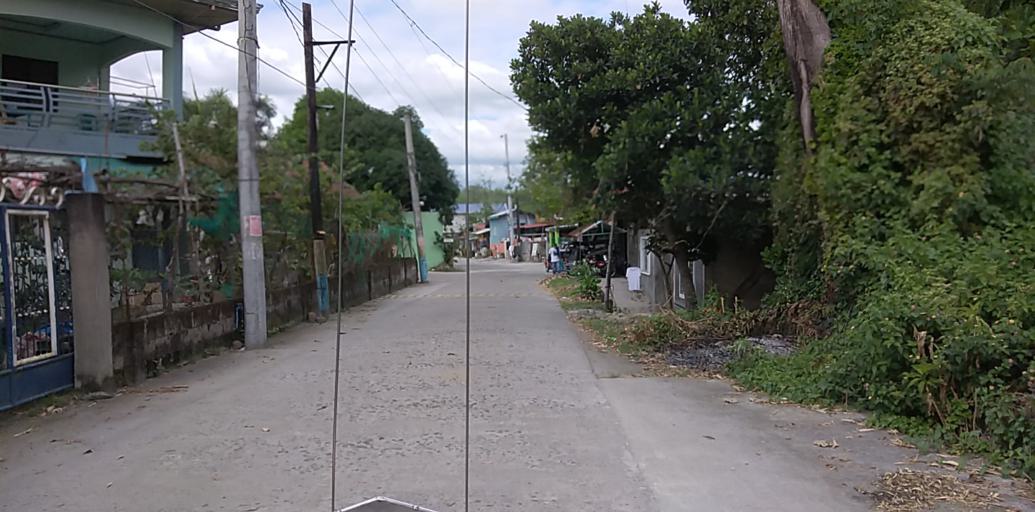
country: PH
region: Central Luzon
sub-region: Province of Pampanga
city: Porac
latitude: 15.0660
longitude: 120.5376
